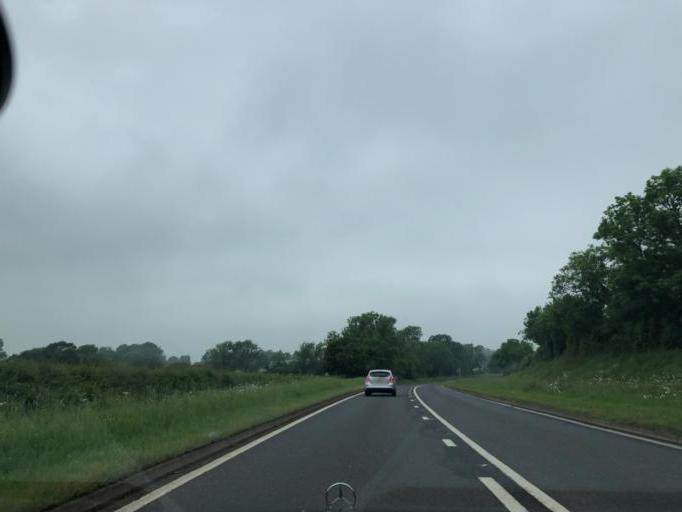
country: GB
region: England
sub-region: Warwickshire
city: Harbury
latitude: 52.2135
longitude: -1.5112
